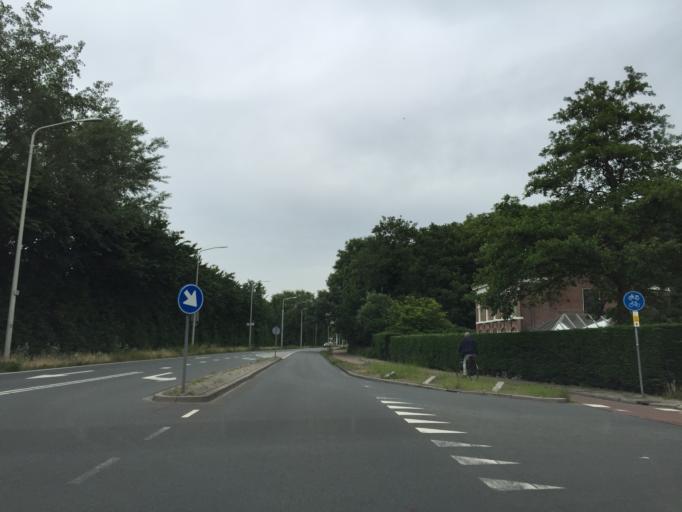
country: NL
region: South Holland
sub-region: Gemeente Westland
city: Poeldijk
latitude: 52.0493
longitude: 4.2227
